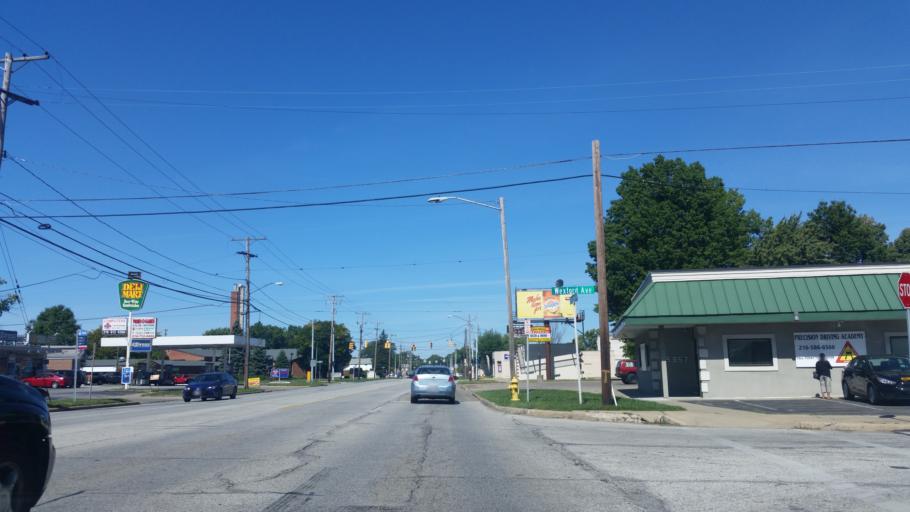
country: US
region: Ohio
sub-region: Cuyahoga County
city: Brooklyn Heights
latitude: 41.4152
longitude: -81.6939
